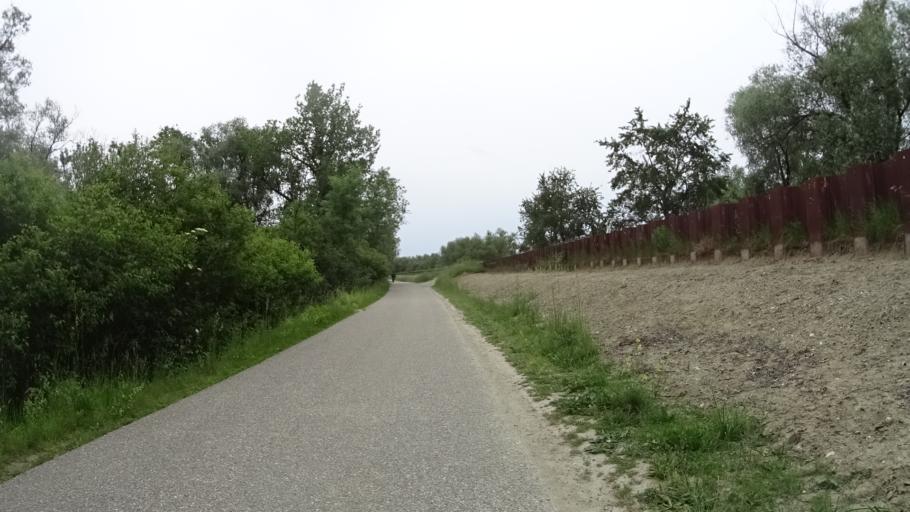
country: DE
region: Bavaria
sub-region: Lower Bavaria
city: Niederalteich
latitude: 48.7777
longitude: 13.0085
